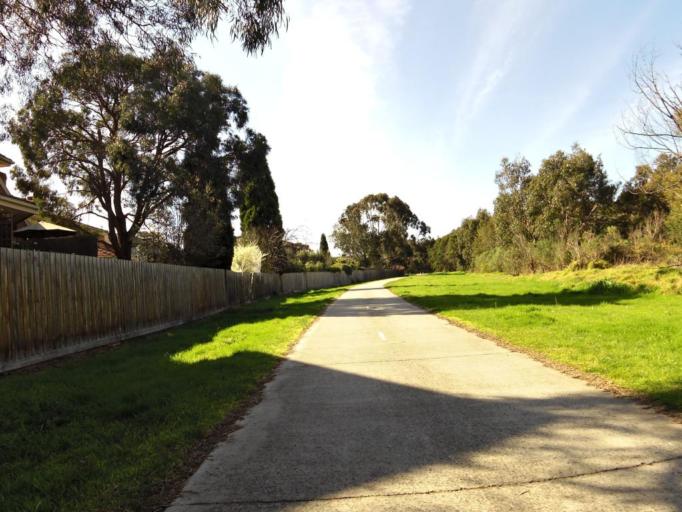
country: AU
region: Victoria
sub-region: Monash
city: Mulgrave
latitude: -37.9116
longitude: 145.2026
